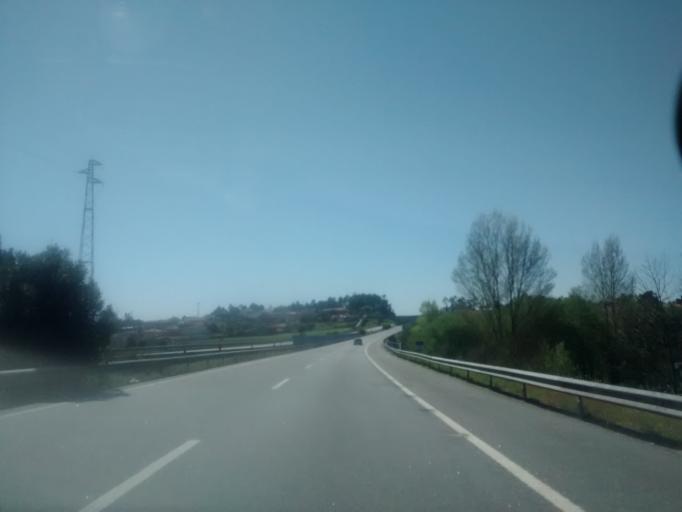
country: PT
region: Braga
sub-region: Vila Nova de Famalicao
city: Vila Nova de Famalicao
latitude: 41.3861
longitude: -8.4859
